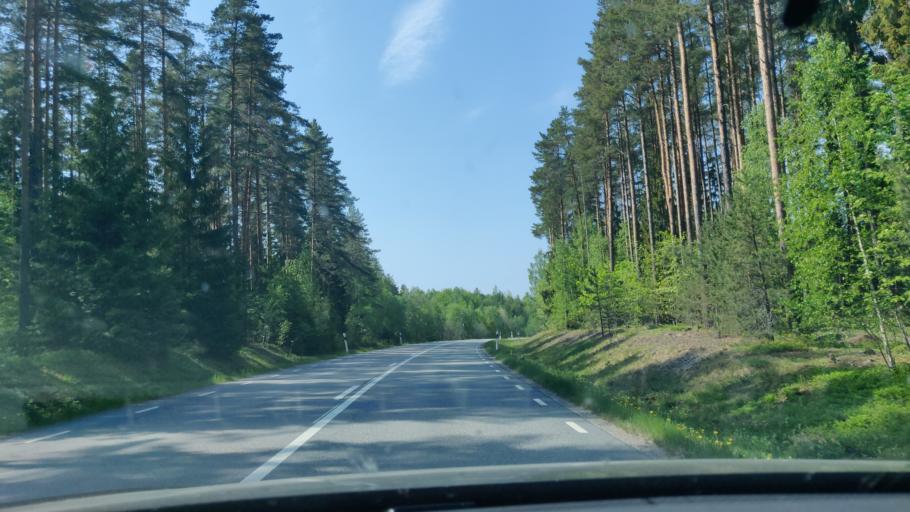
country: SE
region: Uppsala
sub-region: Heby Kommun
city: OEstervala
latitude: 60.1442
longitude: 17.2057
